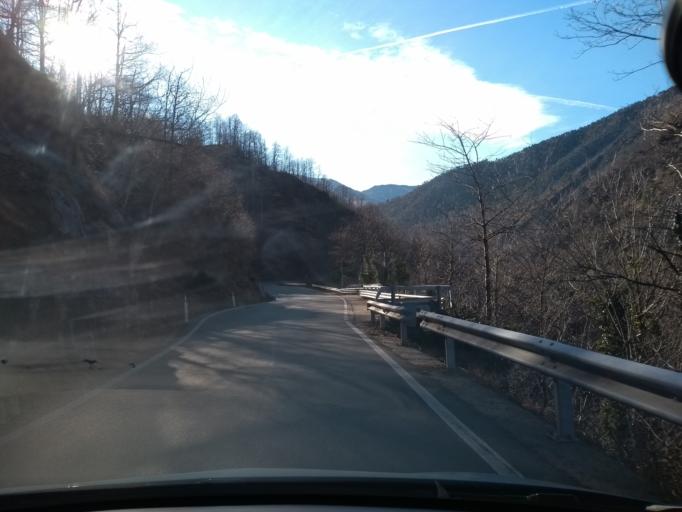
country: IT
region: Piedmont
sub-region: Provincia di Torino
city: La Villa
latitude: 45.2532
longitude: 7.4361
